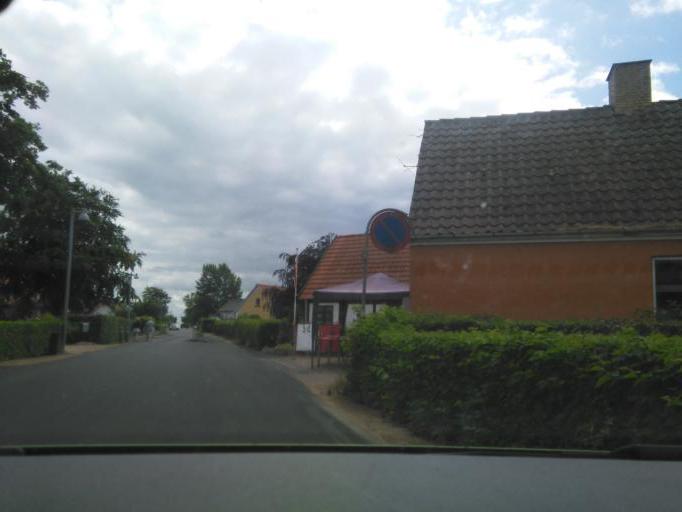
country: DK
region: Zealand
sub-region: Kalundborg Kommune
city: Gorlev
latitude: 55.5231
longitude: 11.1118
